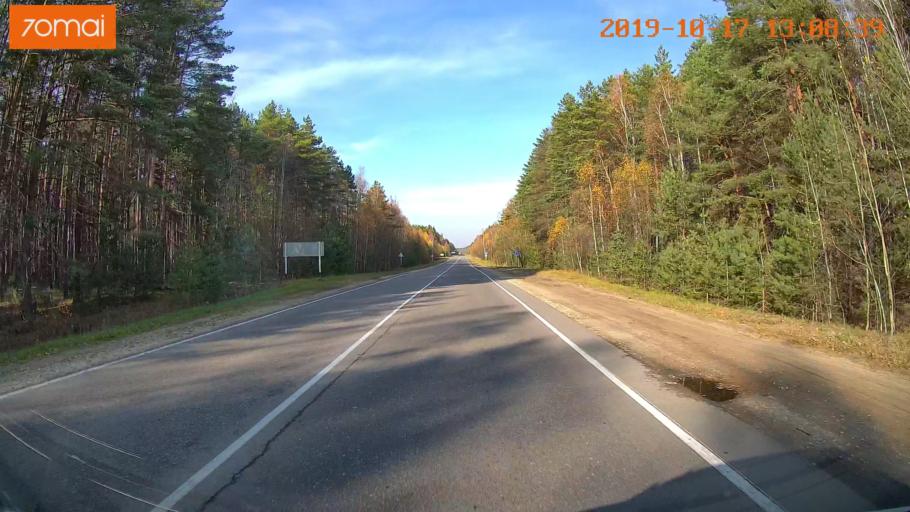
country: RU
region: Rjazan
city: Syntul
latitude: 54.9920
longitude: 41.2679
